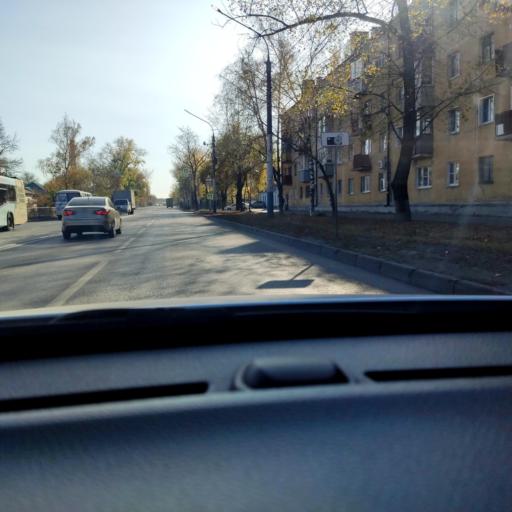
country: RU
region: Voronezj
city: Somovo
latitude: 51.7152
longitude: 39.2747
